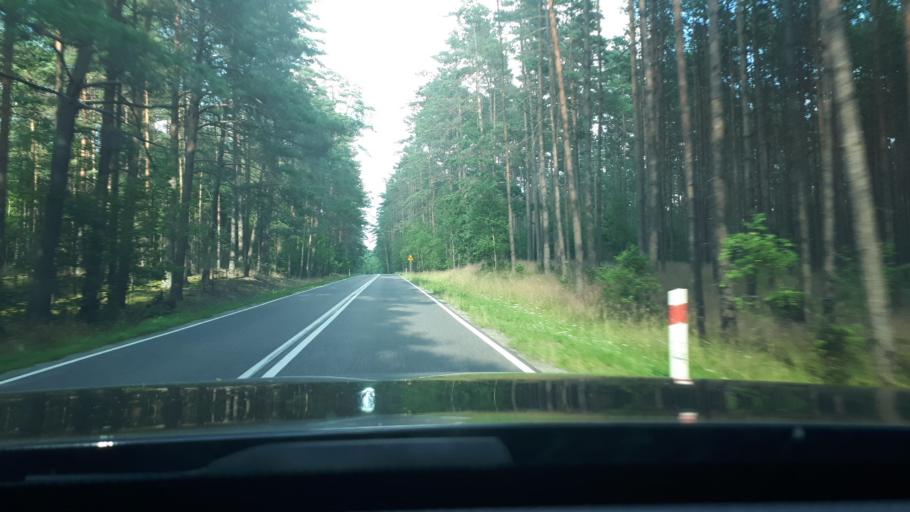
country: PL
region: Warmian-Masurian Voivodeship
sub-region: Powiat olsztynski
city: Stawiguda
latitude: 53.5387
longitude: 20.5359
